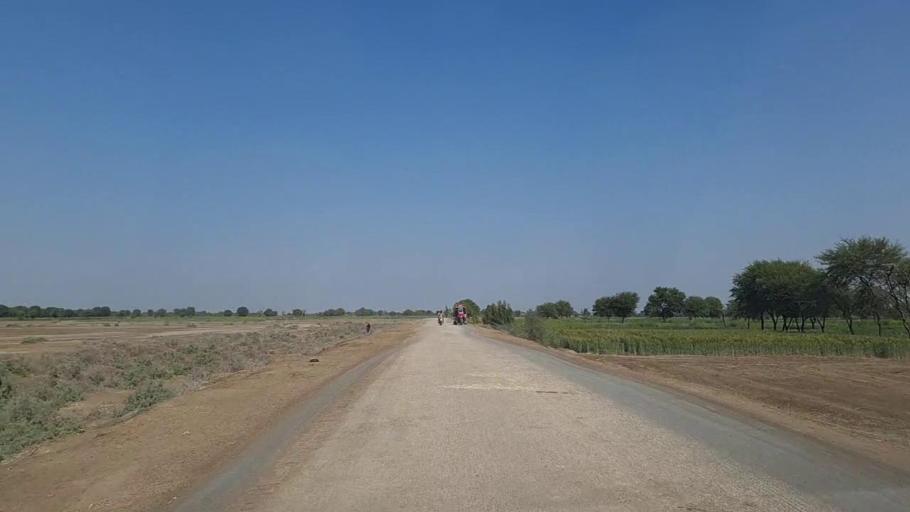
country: PK
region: Sindh
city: Digri
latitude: 25.1645
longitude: 69.1329
